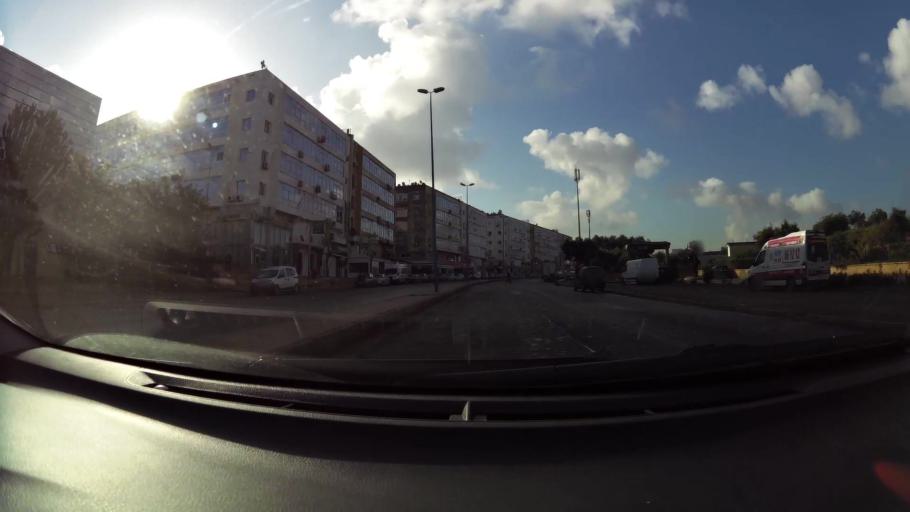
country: MA
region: Grand Casablanca
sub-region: Mediouna
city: Tit Mellil
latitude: 33.6003
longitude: -7.5259
